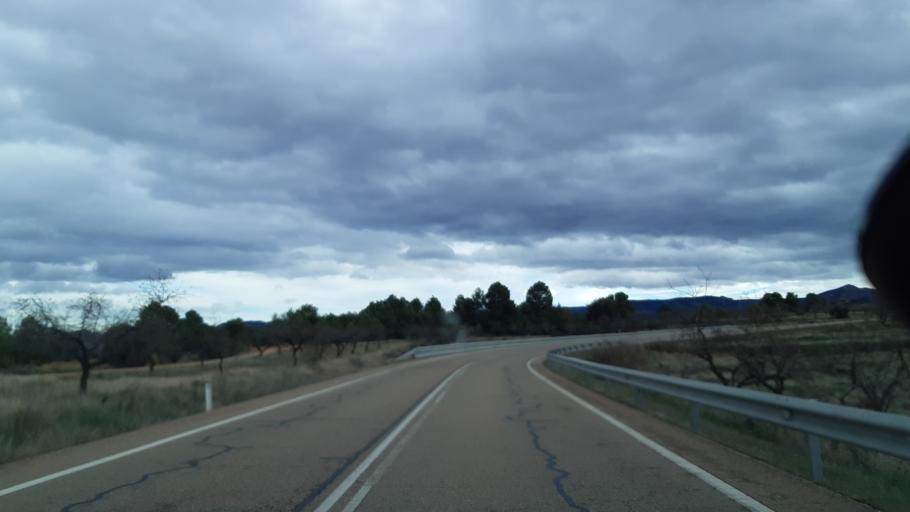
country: ES
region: Aragon
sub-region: Provincia de Teruel
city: Valderrobres
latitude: 40.8994
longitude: 0.1975
